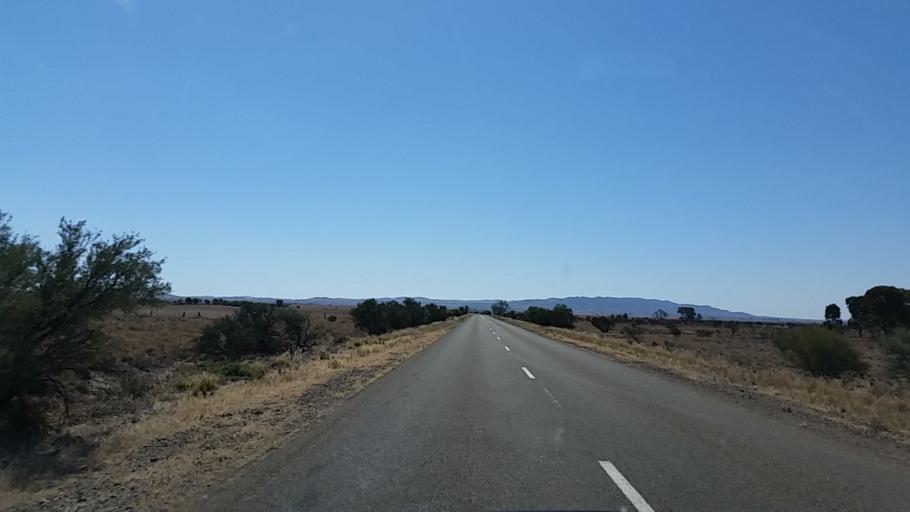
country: AU
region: South Australia
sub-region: Peterborough
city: Peterborough
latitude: -32.6891
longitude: 138.6091
